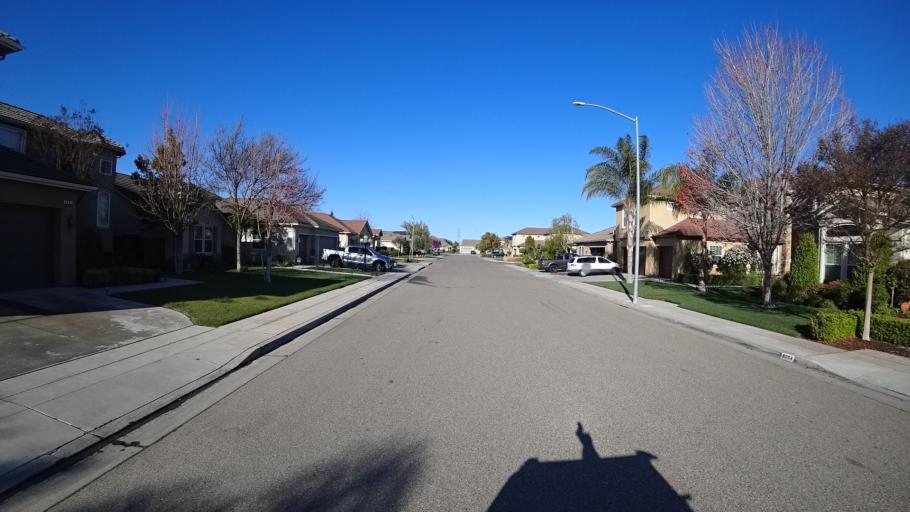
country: US
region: California
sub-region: Fresno County
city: Biola
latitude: 36.8329
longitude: -119.9010
